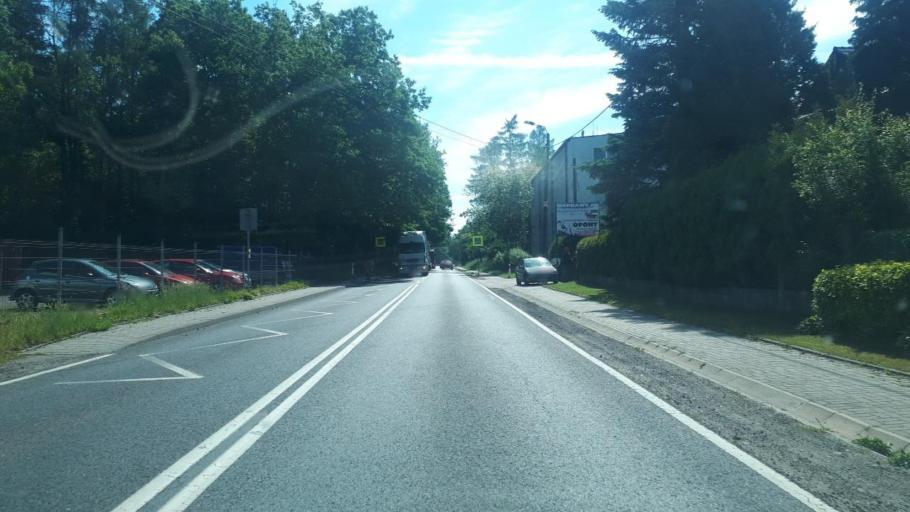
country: PL
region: Silesian Voivodeship
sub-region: Powiat pszczynski
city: Gora
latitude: 49.9754
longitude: 19.1247
